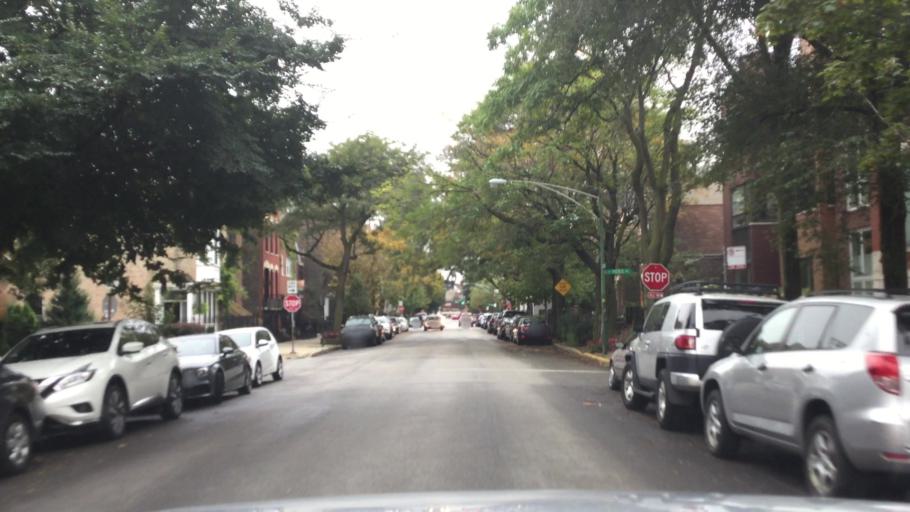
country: US
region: Illinois
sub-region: Cook County
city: Chicago
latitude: 41.9102
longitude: -87.6726
